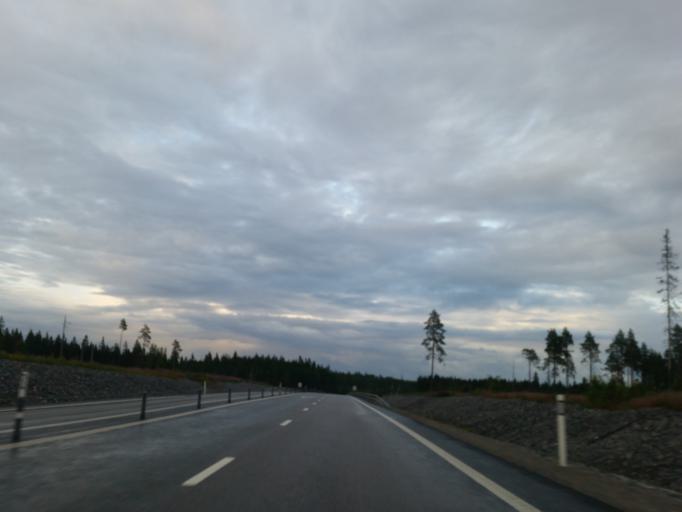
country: SE
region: Vaesterbotten
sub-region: Umea Kommun
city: Umea
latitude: 63.8543
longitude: 20.2696
